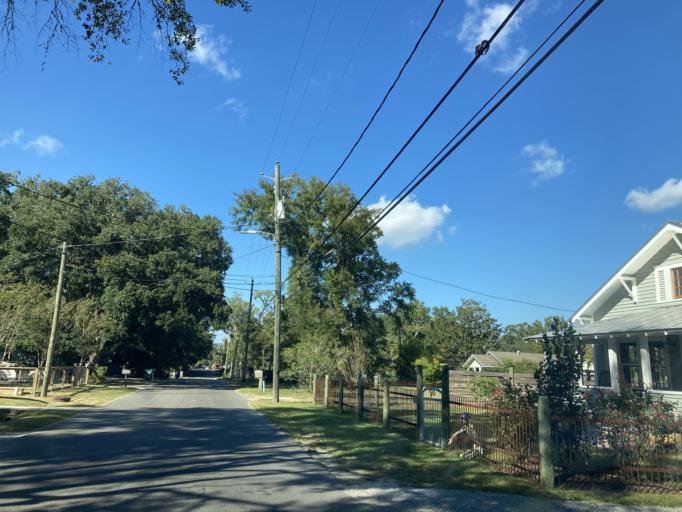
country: US
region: Mississippi
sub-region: Jackson County
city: Ocean Springs
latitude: 30.4066
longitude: -88.8264
